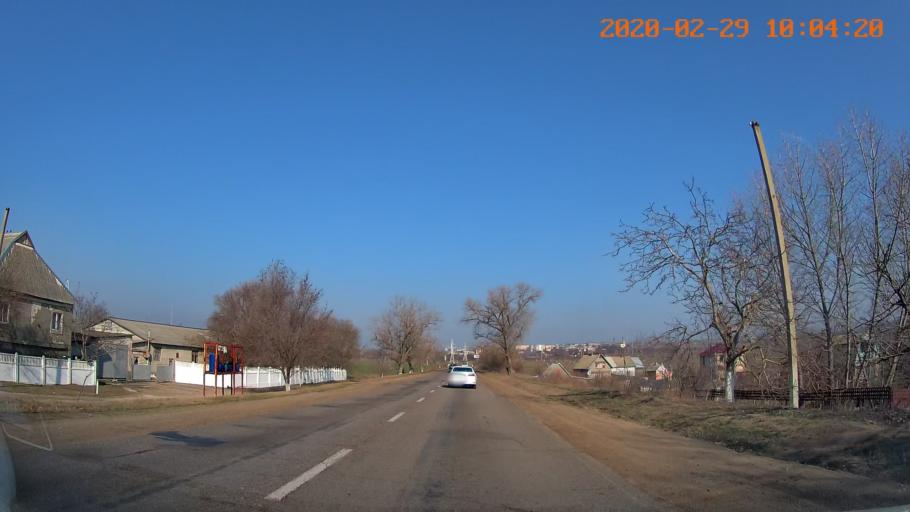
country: MD
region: Causeni
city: Chitcani
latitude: 46.7973
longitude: 29.6761
